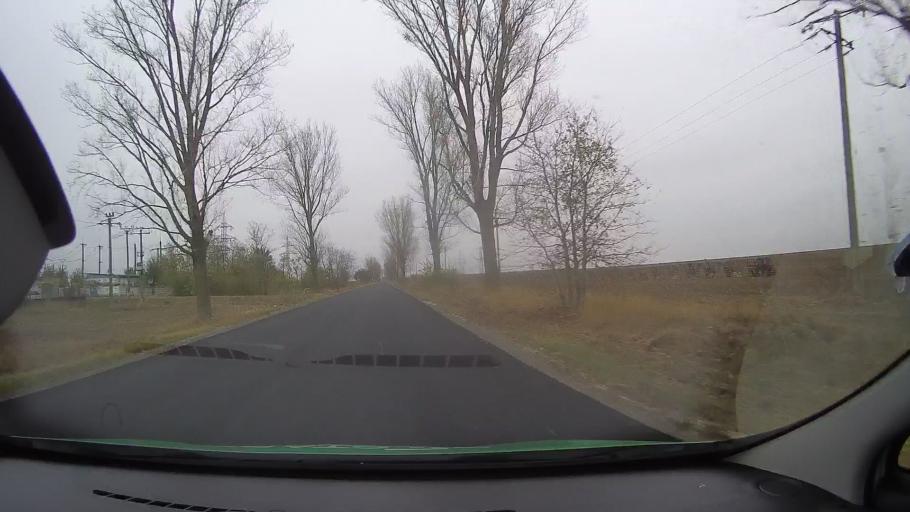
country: RO
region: Ialomita
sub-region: Comuna Valea Ciorii
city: Valea Ciorii
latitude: 44.7507
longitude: 27.5685
